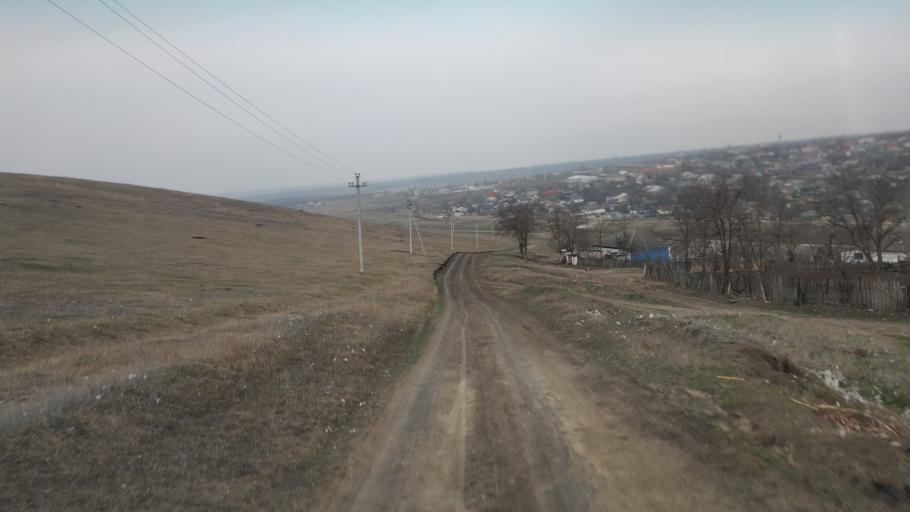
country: MD
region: Chisinau
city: Singera
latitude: 46.8204
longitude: 28.9768
